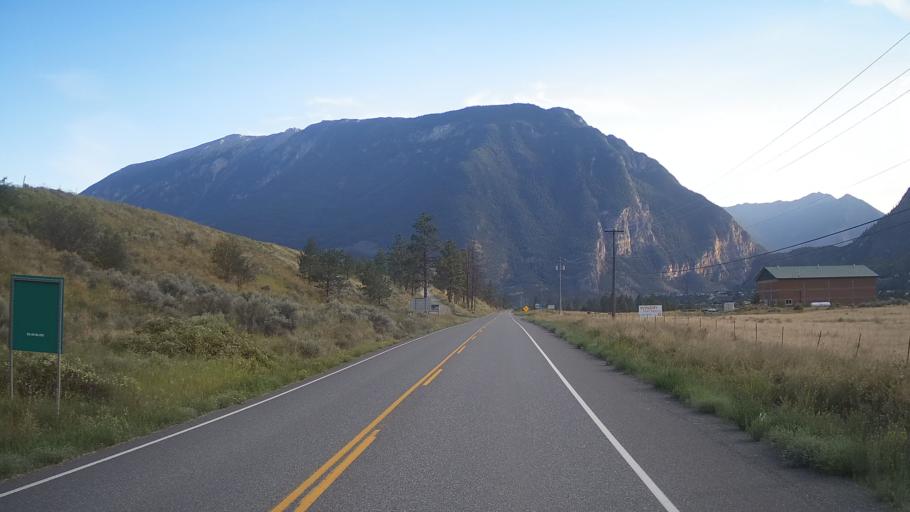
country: CA
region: British Columbia
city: Lillooet
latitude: 50.7007
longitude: -121.9154
